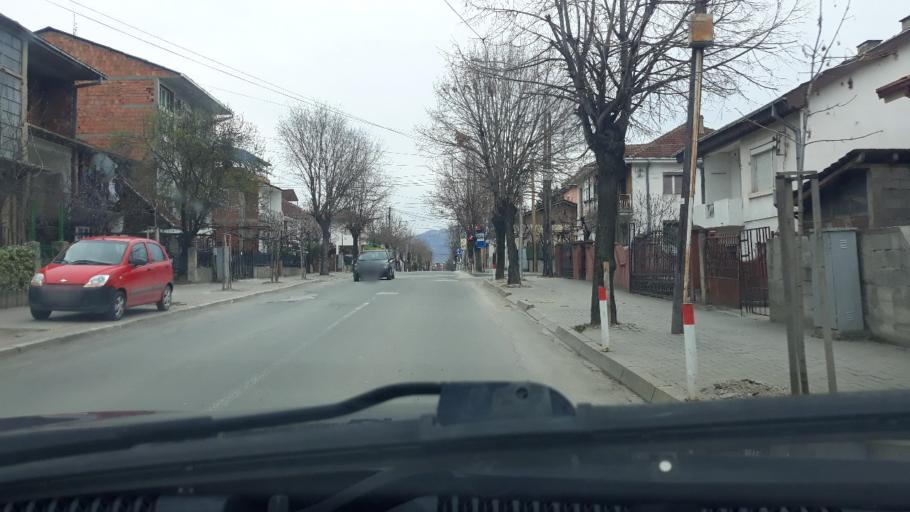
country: MK
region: Kavadarci
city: Kavadarci
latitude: 41.4325
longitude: 22.0080
